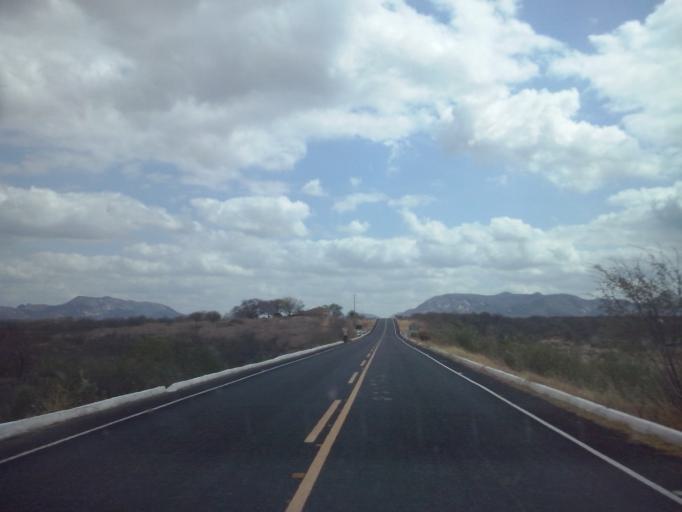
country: BR
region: Paraiba
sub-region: Pombal
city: Pombal
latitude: -6.8336
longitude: -37.5688
